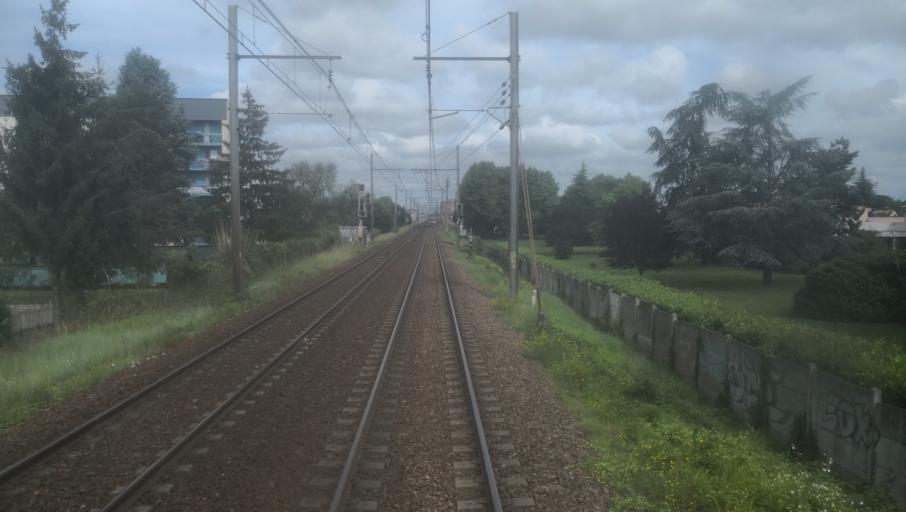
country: FR
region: Aquitaine
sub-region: Departement du Lot-et-Garonne
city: Marmande
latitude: 44.4992
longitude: 0.1750
